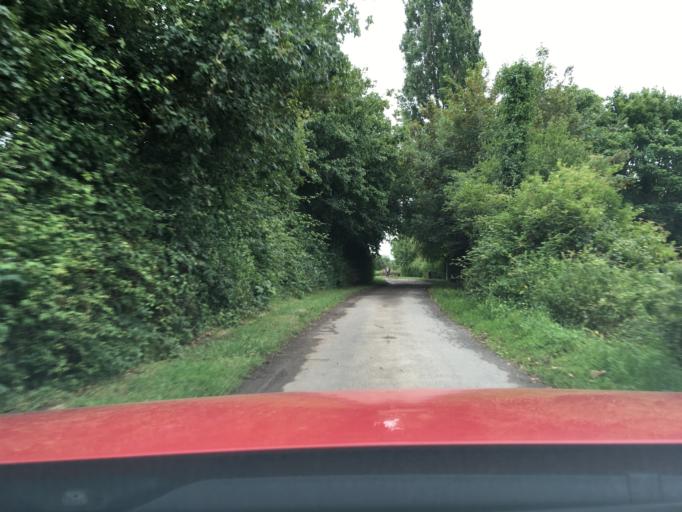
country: GB
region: England
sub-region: Gloucestershire
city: Cinderford
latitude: 51.7895
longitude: -2.4283
